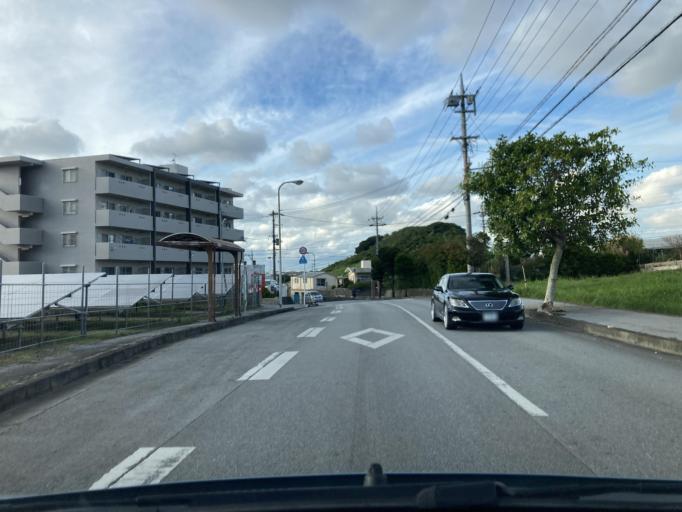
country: JP
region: Okinawa
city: Tomigusuku
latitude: 26.1449
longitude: 127.7328
